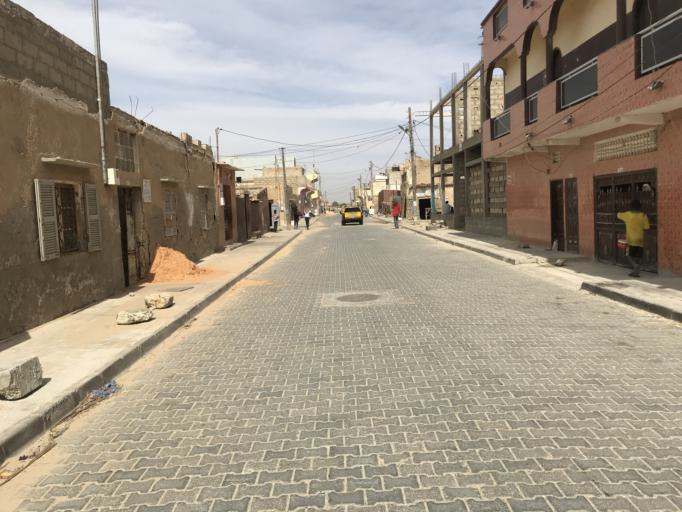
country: SN
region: Saint-Louis
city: Saint-Louis
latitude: 16.0229
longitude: -16.4851
